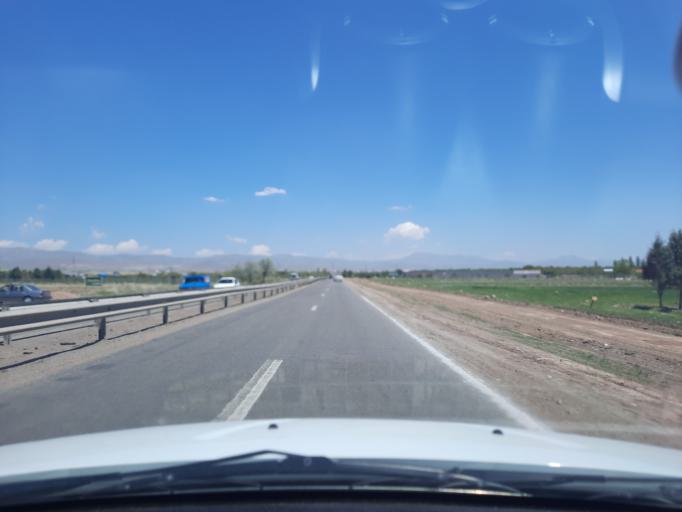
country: IR
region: Qazvin
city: Alvand
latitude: 36.2709
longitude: 50.0973
